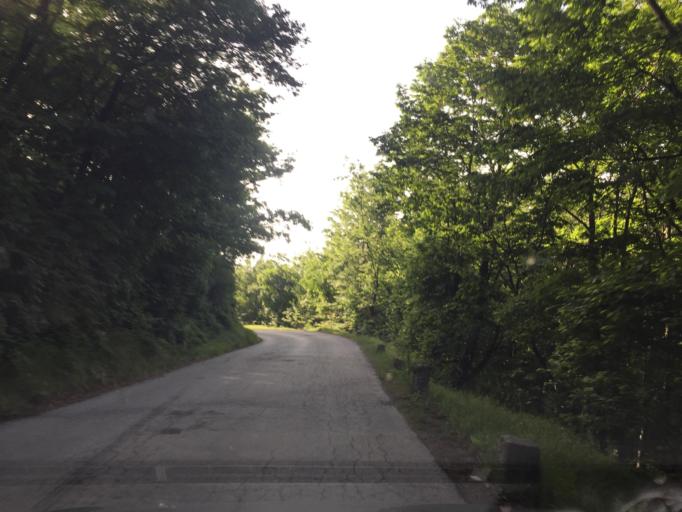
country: HR
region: Istarska
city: Buzet
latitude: 45.4728
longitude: 14.0958
